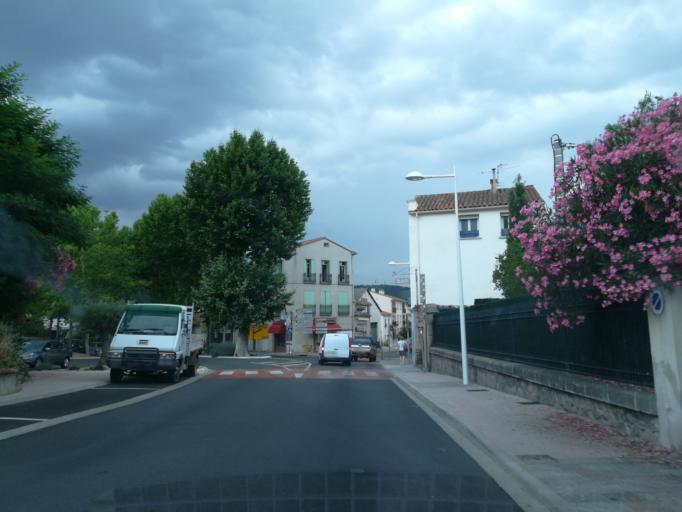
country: FR
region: Languedoc-Roussillon
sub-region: Departement des Pyrenees-Orientales
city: Ceret
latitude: 42.4923
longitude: 2.7433
